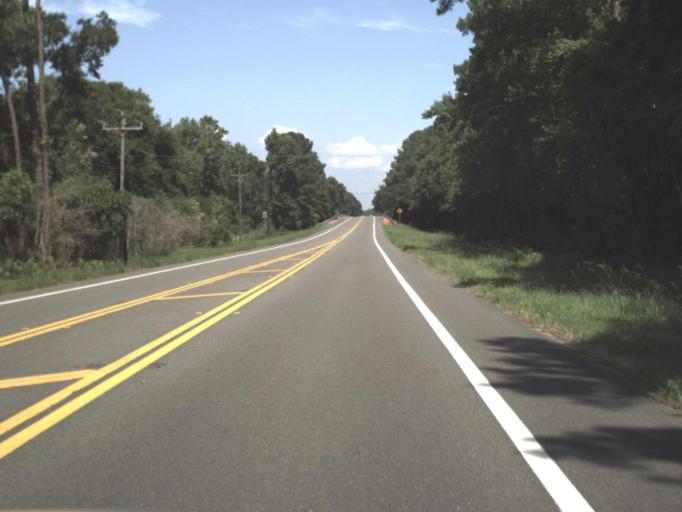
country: US
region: Florida
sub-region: Clay County
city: Green Cove Springs
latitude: 29.9836
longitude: -81.5623
